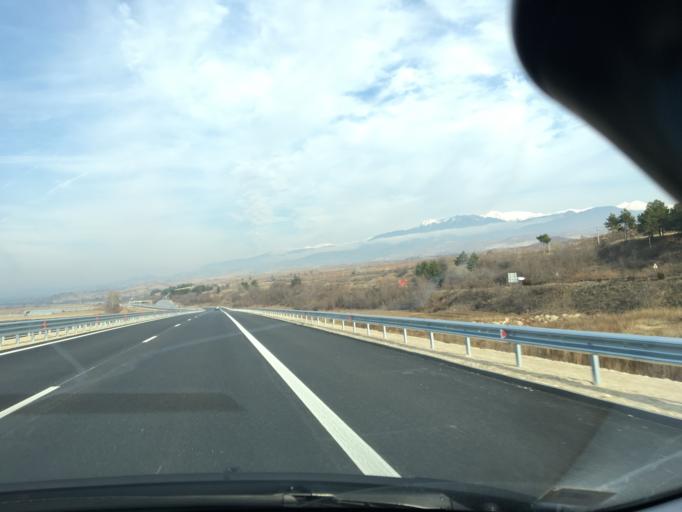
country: BG
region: Blagoevgrad
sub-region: Obshtina Sandanski
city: Sandanski
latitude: 41.5645
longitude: 23.2408
